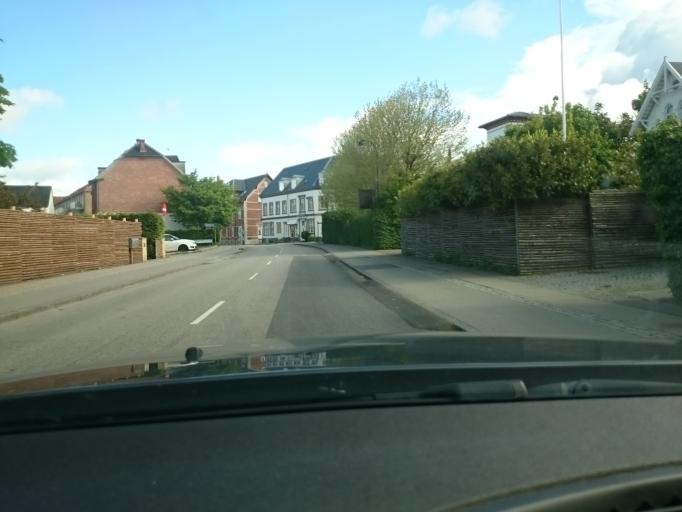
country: DK
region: Capital Region
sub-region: Gentofte Kommune
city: Charlottenlund
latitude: 55.7569
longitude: 12.5758
